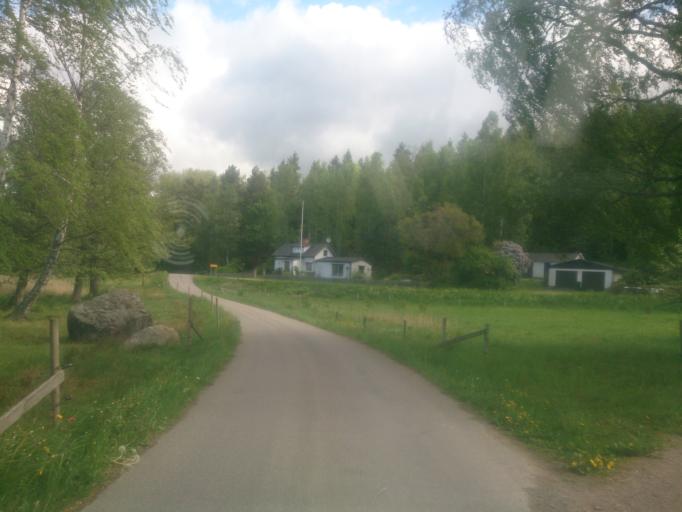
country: SE
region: OEstergoetland
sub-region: Atvidabergs Kommun
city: Atvidaberg
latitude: 58.3065
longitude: 16.0766
